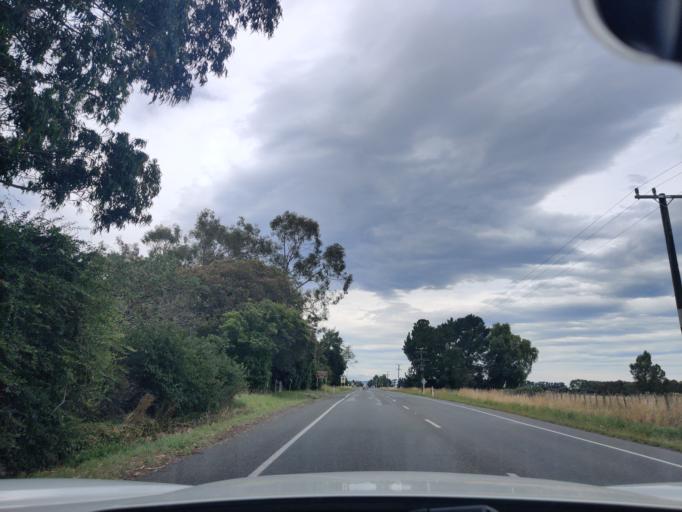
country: NZ
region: Wellington
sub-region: Masterton District
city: Masterton
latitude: -40.9840
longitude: 175.5808
